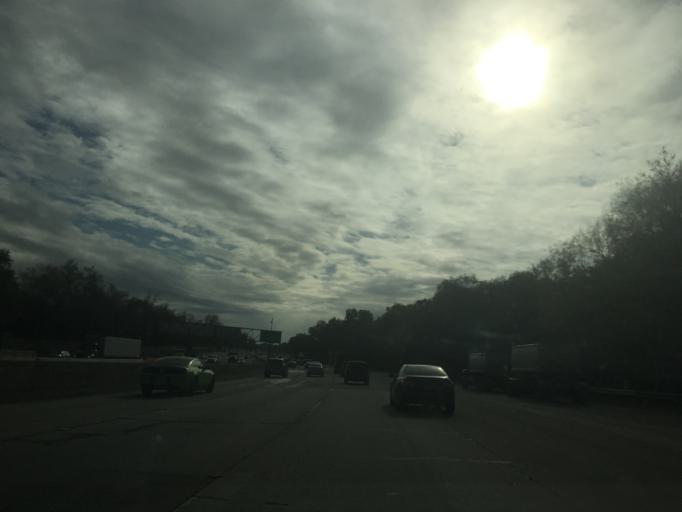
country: US
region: California
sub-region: Yolo County
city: West Sacramento
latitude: 38.5613
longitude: -121.5153
